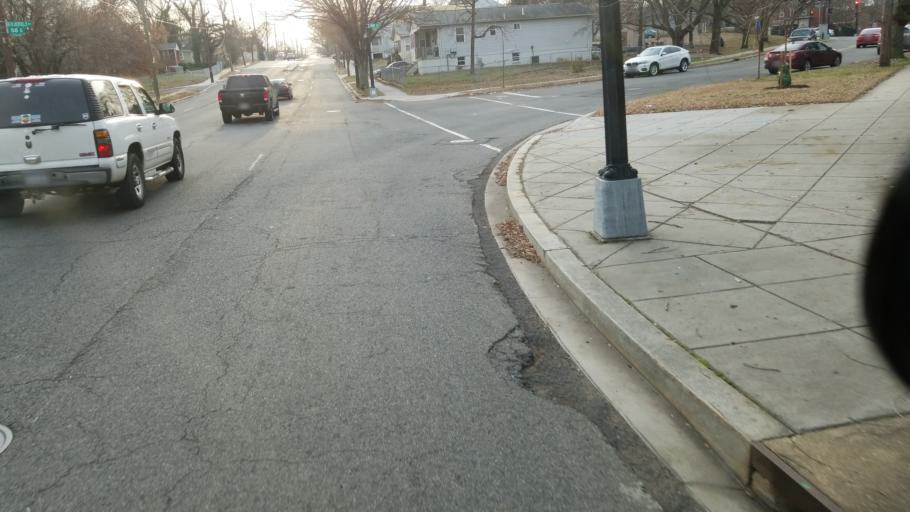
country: US
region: Maryland
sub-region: Prince George's County
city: Fairmount Heights
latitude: 38.8995
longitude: -76.9179
